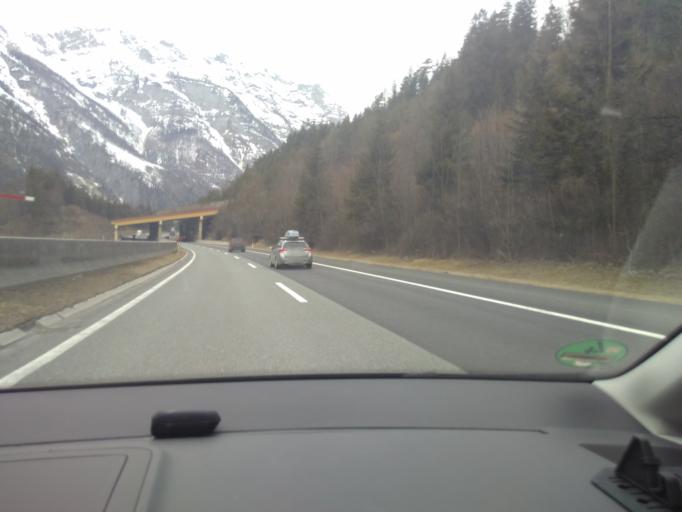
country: AT
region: Salzburg
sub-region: Politischer Bezirk Sankt Johann im Pongau
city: Werfen
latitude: 47.5039
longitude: 13.1777
